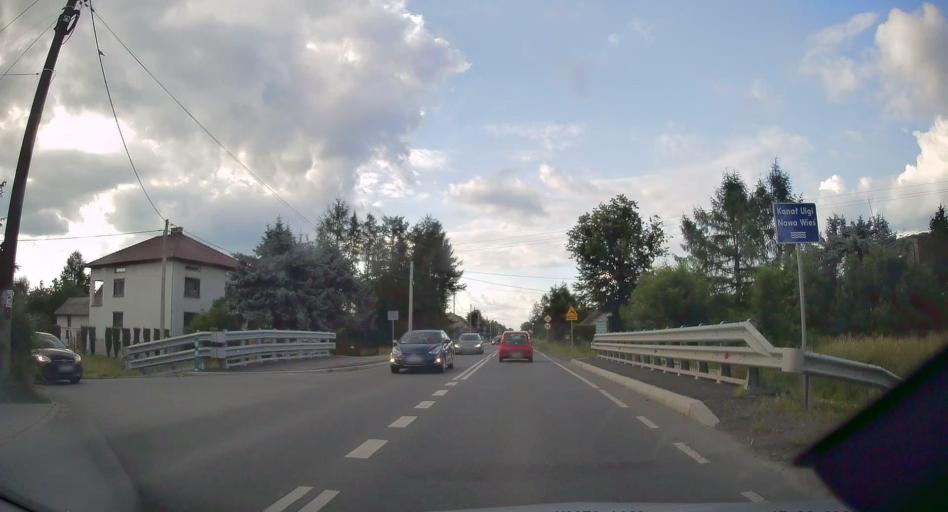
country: PL
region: Lesser Poland Voivodeship
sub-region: Powiat oswiecimski
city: Nowa Wies
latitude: 49.8996
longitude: 19.2179
